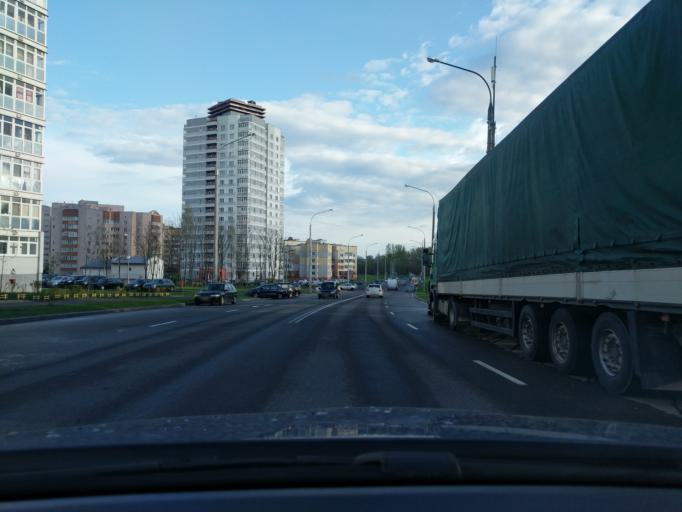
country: BY
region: Minsk
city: Novoye Medvezhino
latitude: 53.8970
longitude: 27.4748
